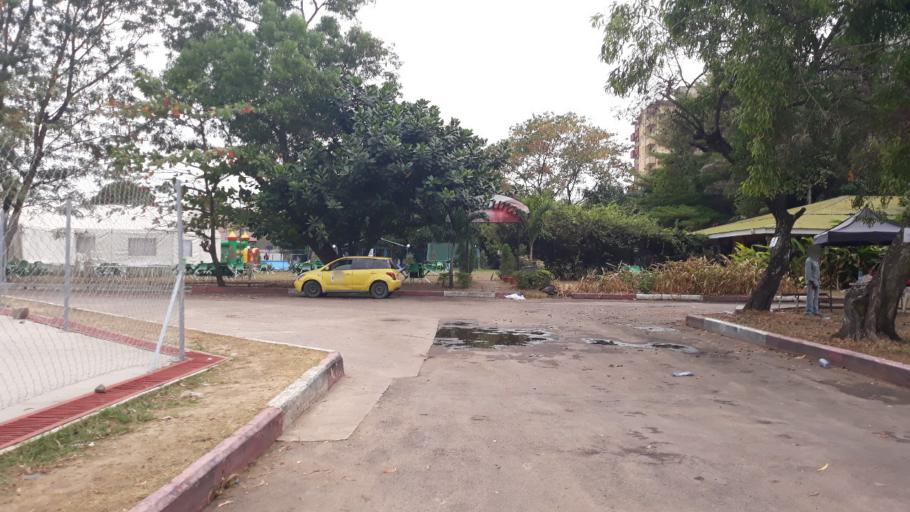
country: CD
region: Kinshasa
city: Kinshasa
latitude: -4.3295
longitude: 15.2754
